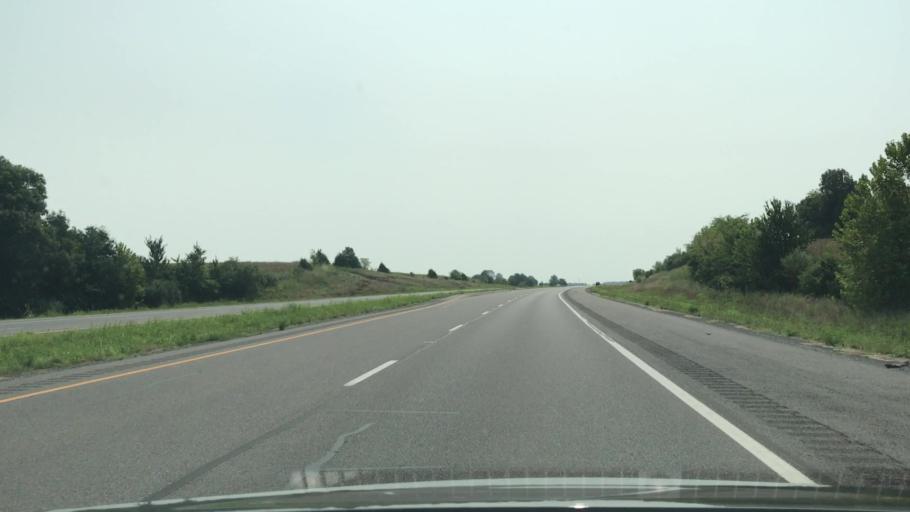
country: US
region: Kentucky
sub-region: Graves County
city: Mayfield
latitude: 36.6908
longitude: -88.5528
